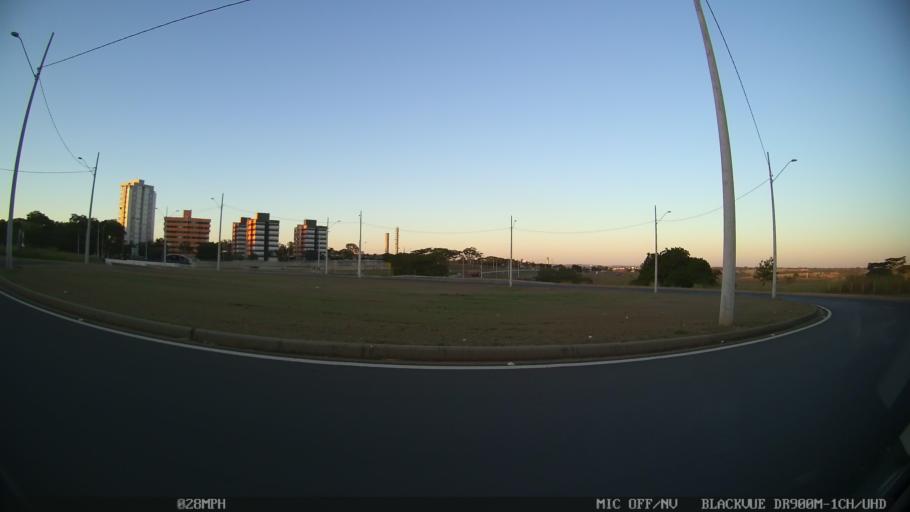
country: BR
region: Sao Paulo
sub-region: Sao Jose Do Rio Preto
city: Sao Jose do Rio Preto
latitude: -20.8513
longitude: -49.3924
